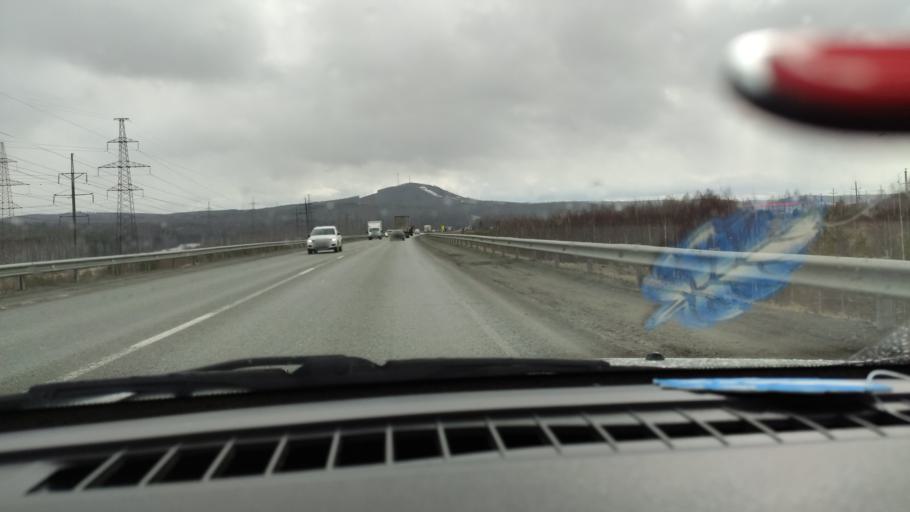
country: RU
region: Sverdlovsk
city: Revda
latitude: 56.8278
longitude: 59.9513
